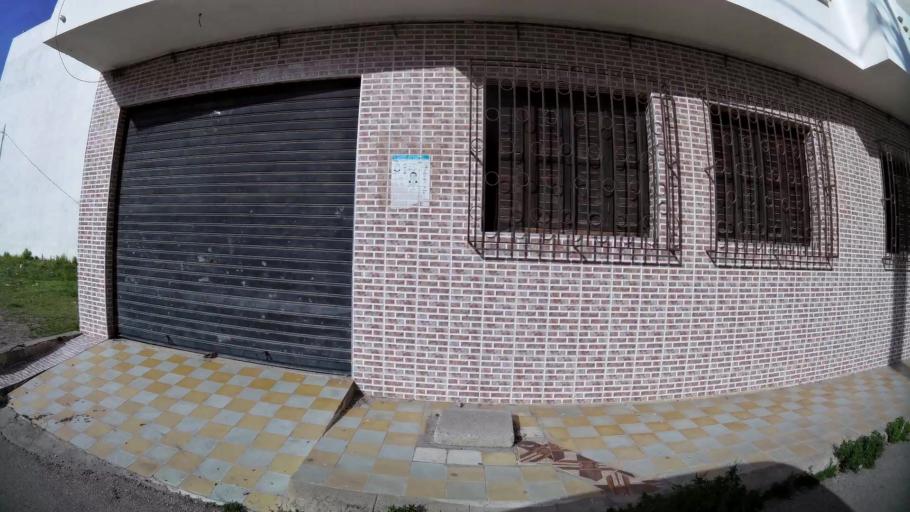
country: MA
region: Tanger-Tetouan
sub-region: Tetouan
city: Martil
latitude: 35.6108
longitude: -5.2830
